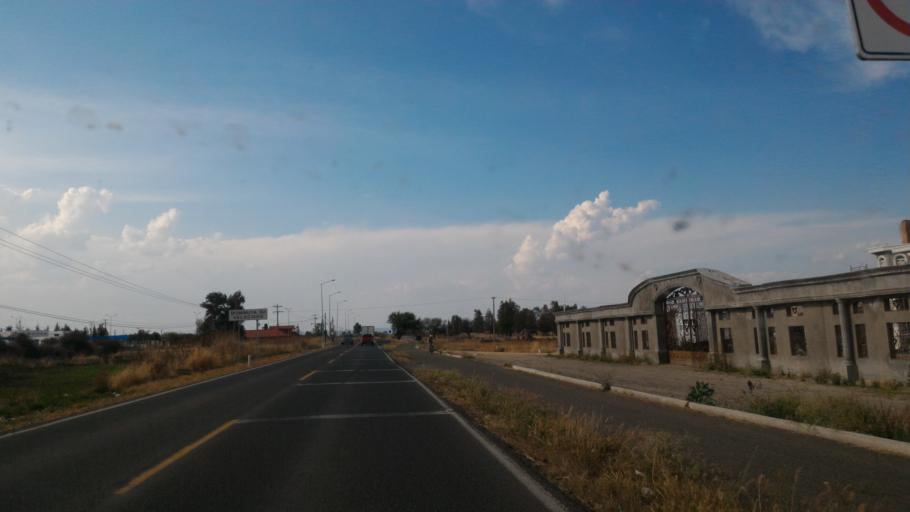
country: MX
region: Guanajuato
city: Ciudad Manuel Doblado
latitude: 20.7541
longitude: -101.9640
